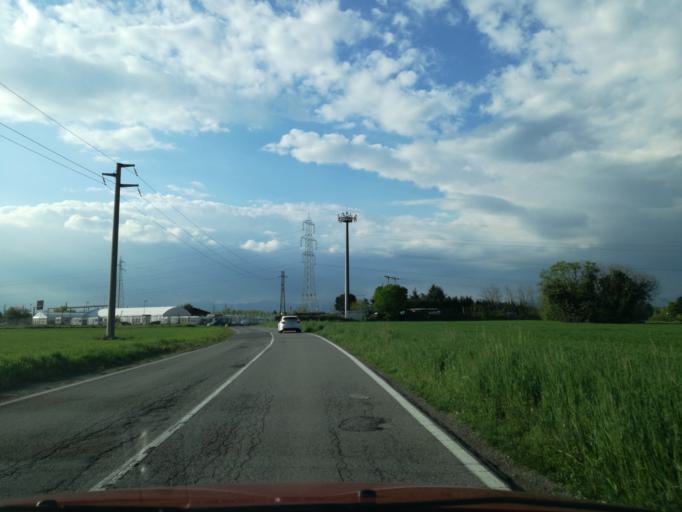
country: IT
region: Lombardy
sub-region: Provincia di Monza e Brianza
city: Velasca
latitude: 45.6358
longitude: 9.3659
